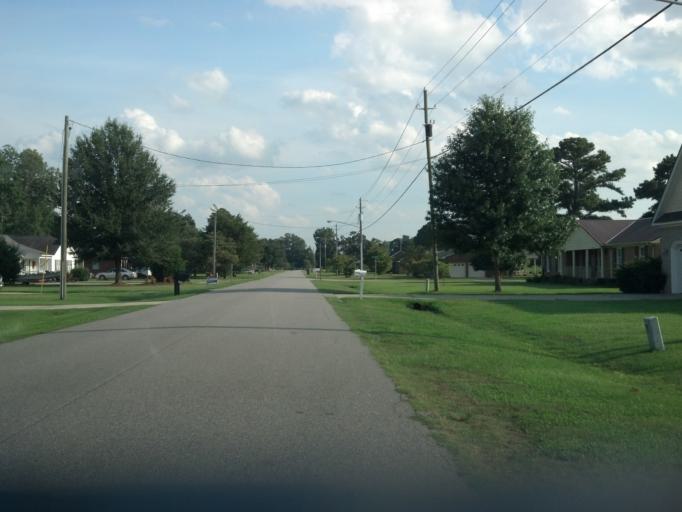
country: US
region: North Carolina
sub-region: Pitt County
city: Ayden
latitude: 35.4797
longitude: -77.4104
